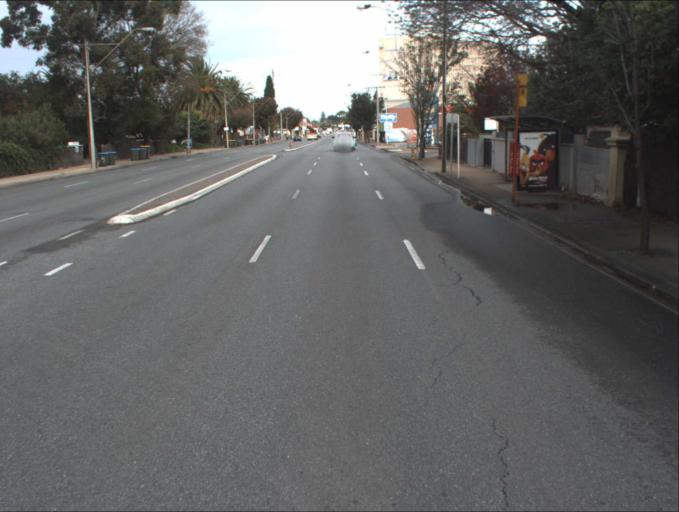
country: AU
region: South Australia
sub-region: Port Adelaide Enfield
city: Klemzig
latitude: -34.8861
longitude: 138.6175
